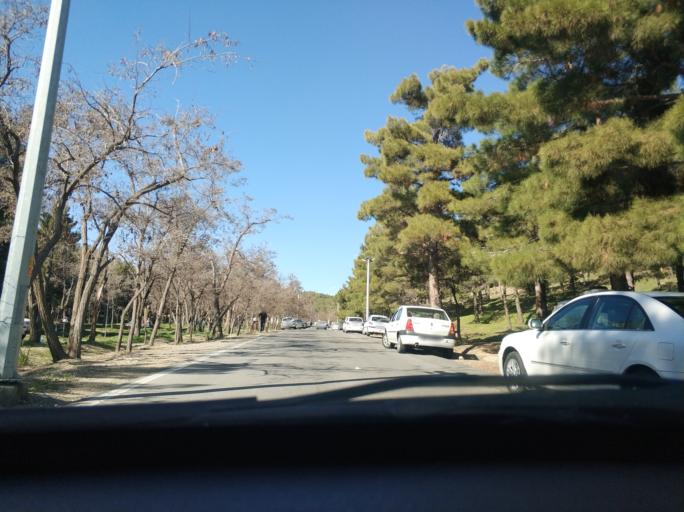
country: IR
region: Tehran
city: Tajrish
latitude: 35.7867
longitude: 51.5588
